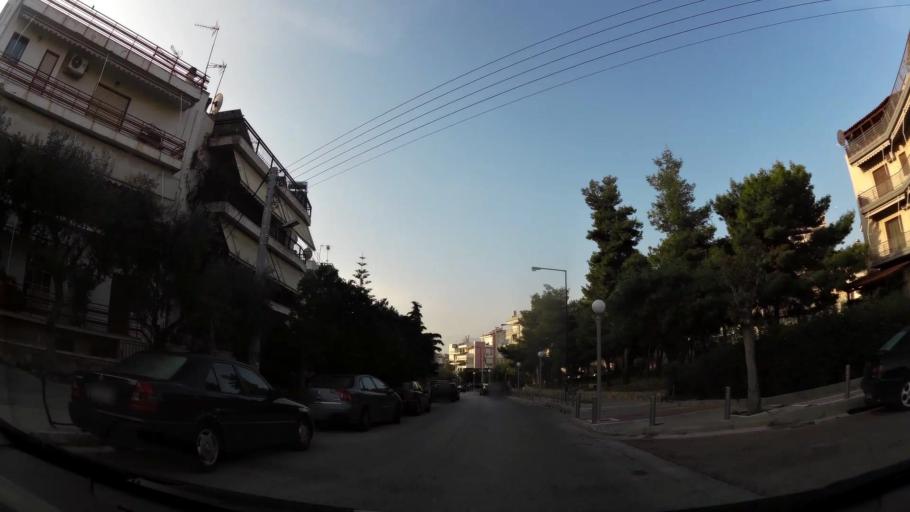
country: GR
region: Attica
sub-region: Nomarchia Athinas
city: Ymittos
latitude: 37.9458
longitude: 23.7468
